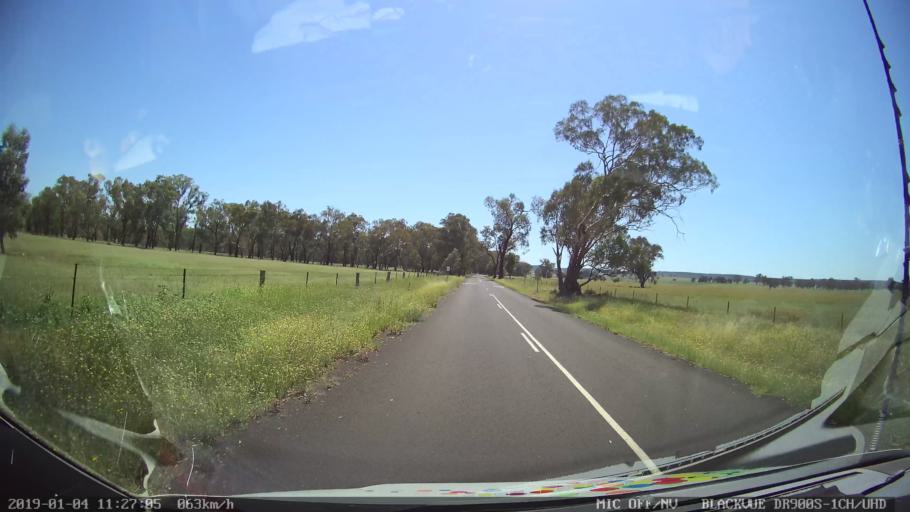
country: AU
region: New South Wales
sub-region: Cabonne
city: Molong
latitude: -33.1111
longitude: 148.7588
